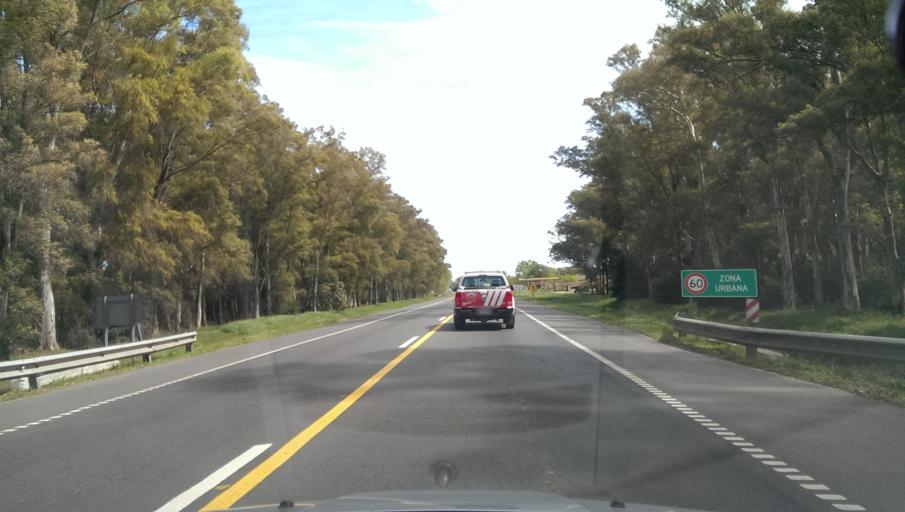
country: AR
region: Buenos Aires
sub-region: Partido de Las Flores
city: Las Flores
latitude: -36.3832
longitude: -59.4869
